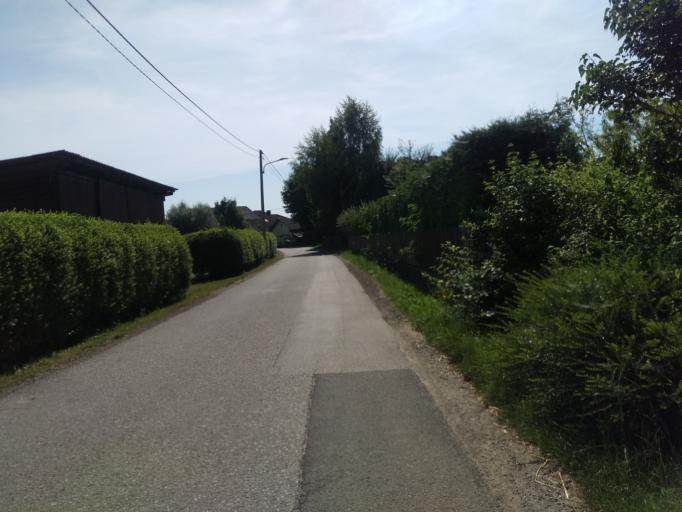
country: AT
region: Styria
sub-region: Politischer Bezirk Graz-Umgebung
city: Gossendorf
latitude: 46.9933
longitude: 15.4806
